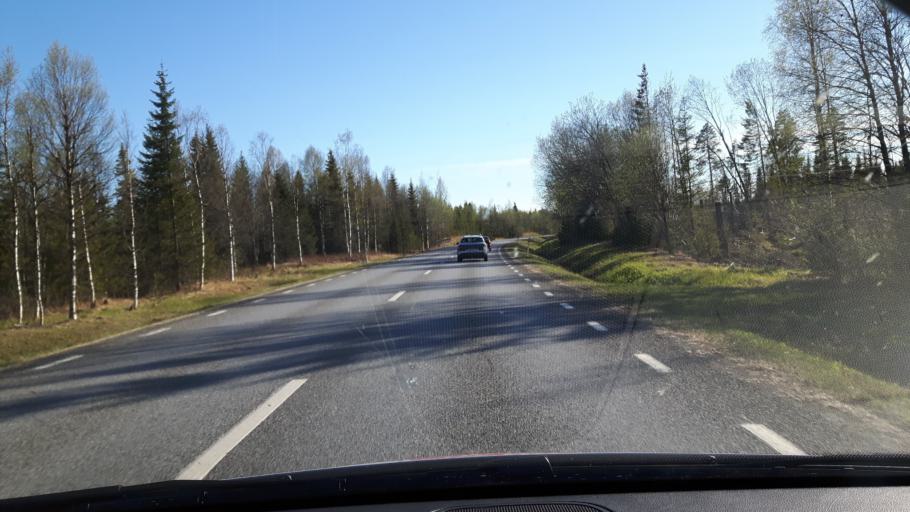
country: SE
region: Jaemtland
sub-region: OEstersunds Kommun
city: Lit
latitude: 63.4186
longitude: 15.1042
